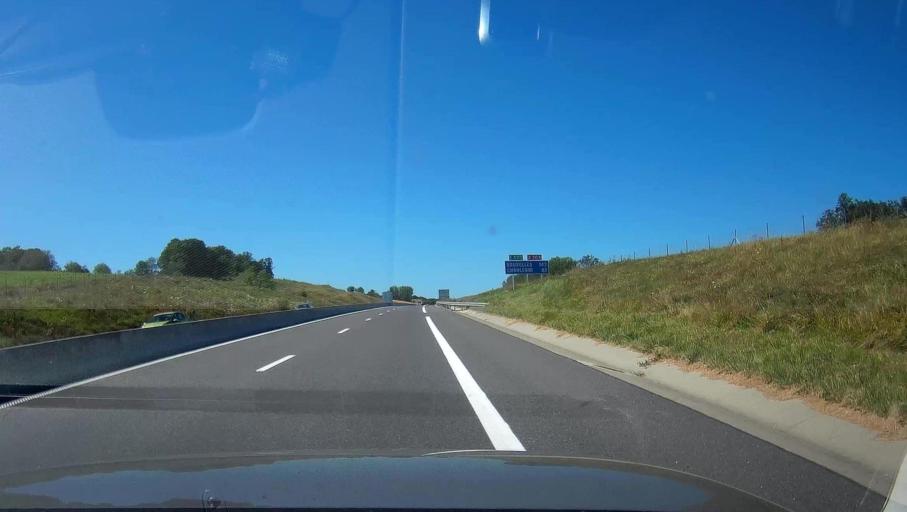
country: FR
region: Champagne-Ardenne
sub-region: Departement des Ardennes
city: Tournes
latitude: 49.7712
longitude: 4.6281
